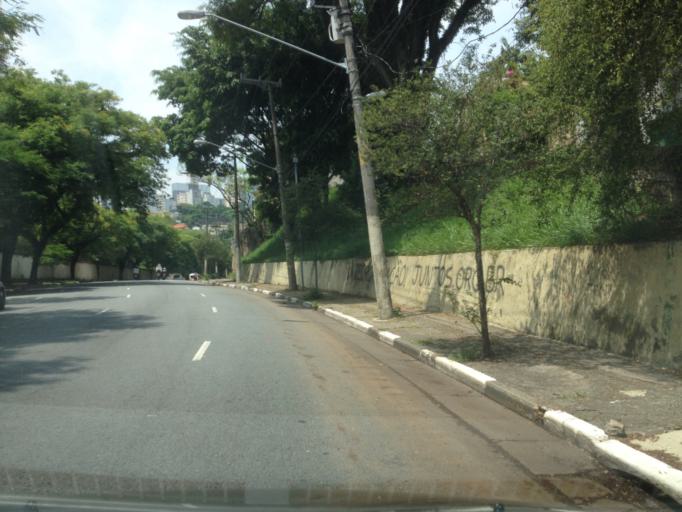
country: BR
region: Sao Paulo
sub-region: Sao Paulo
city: Sao Paulo
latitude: -23.5494
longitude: -46.6662
